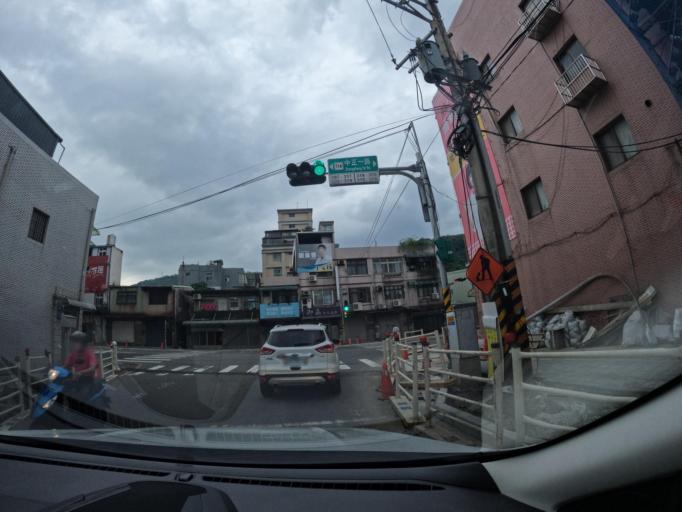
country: TW
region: Taiwan
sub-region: Taoyuan
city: Taoyuan
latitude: 24.9569
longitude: 121.3569
